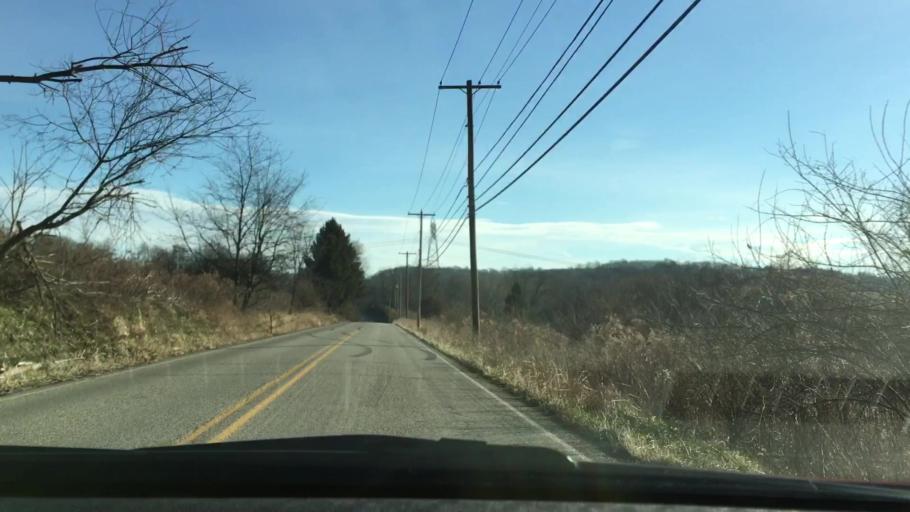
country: US
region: Pennsylvania
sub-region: Westmoreland County
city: Irwin
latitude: 40.2652
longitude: -79.6886
